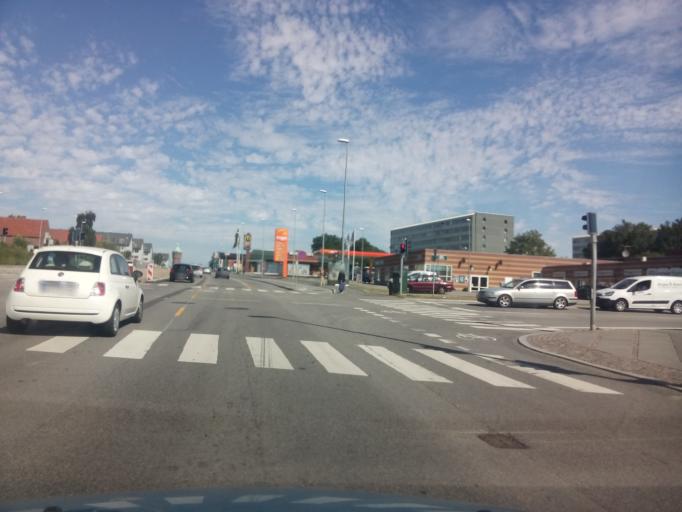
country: DK
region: Central Jutland
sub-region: Arhus Kommune
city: Arhus
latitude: 56.1782
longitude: 10.2006
